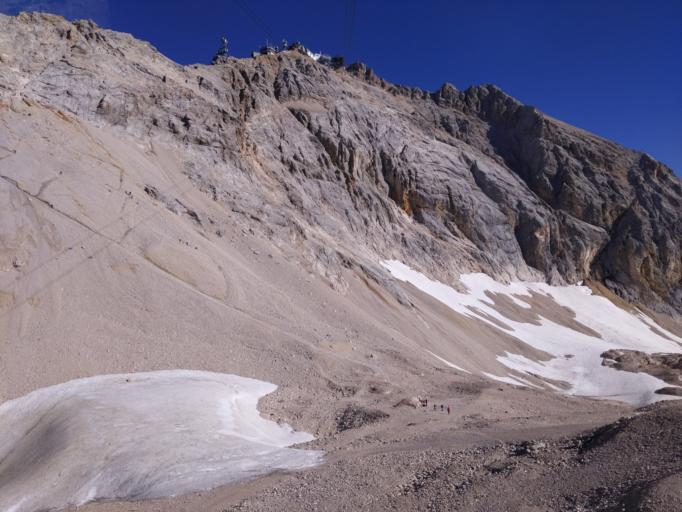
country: AT
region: Tyrol
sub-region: Politischer Bezirk Reutte
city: Ehrwald
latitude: 47.4141
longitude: 10.9804
